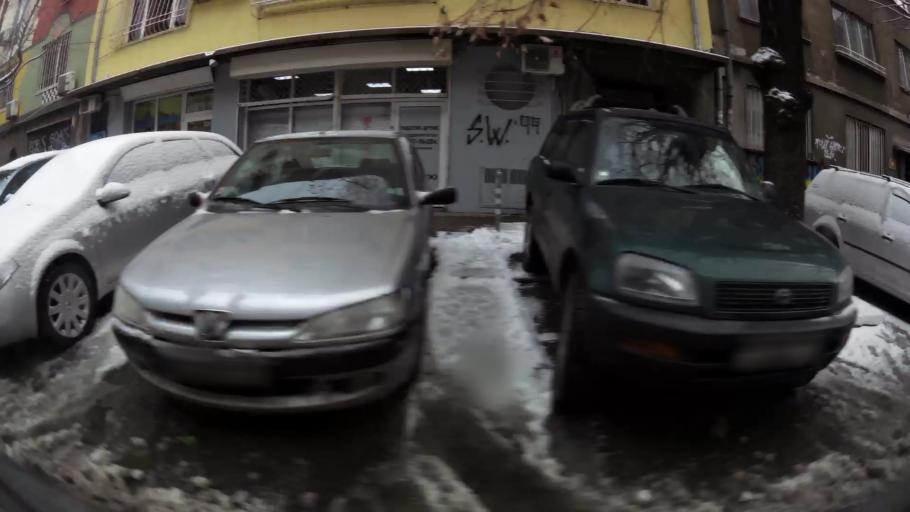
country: BG
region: Sofia-Capital
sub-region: Stolichna Obshtina
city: Sofia
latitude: 42.6871
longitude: 23.3287
